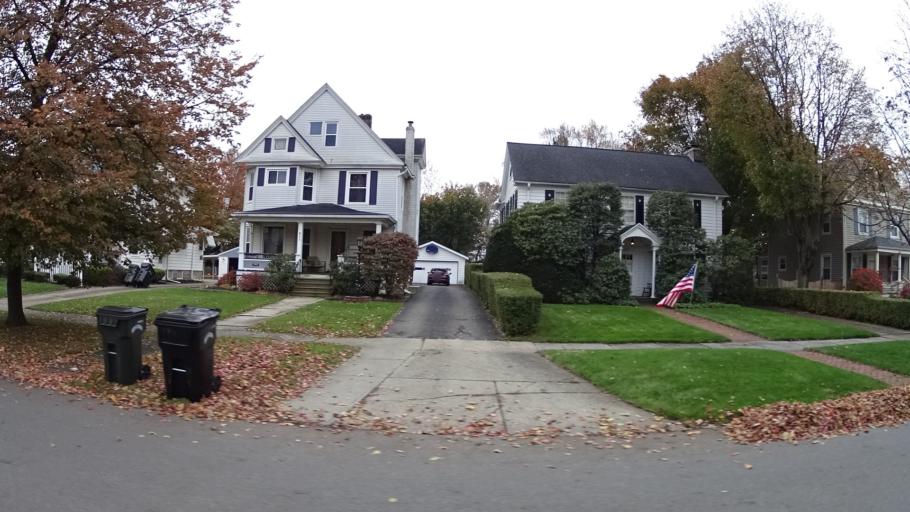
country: US
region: Ohio
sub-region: Lorain County
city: Elyria
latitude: 41.3631
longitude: -82.0972
